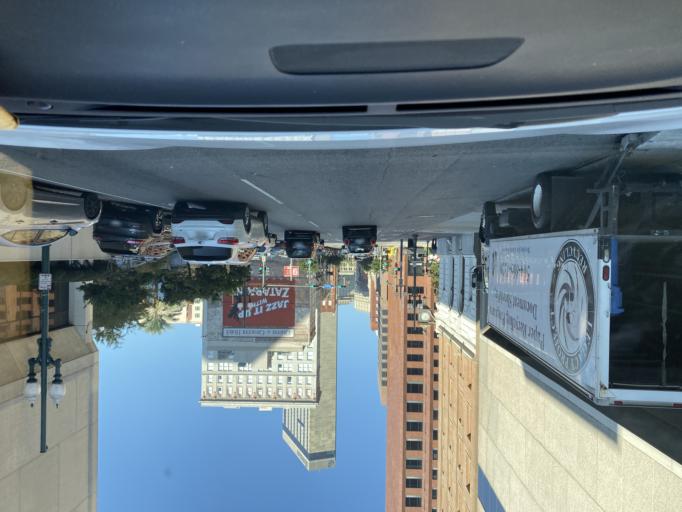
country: US
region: Louisiana
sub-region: Orleans Parish
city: New Orleans
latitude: 29.9486
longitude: -90.0696
